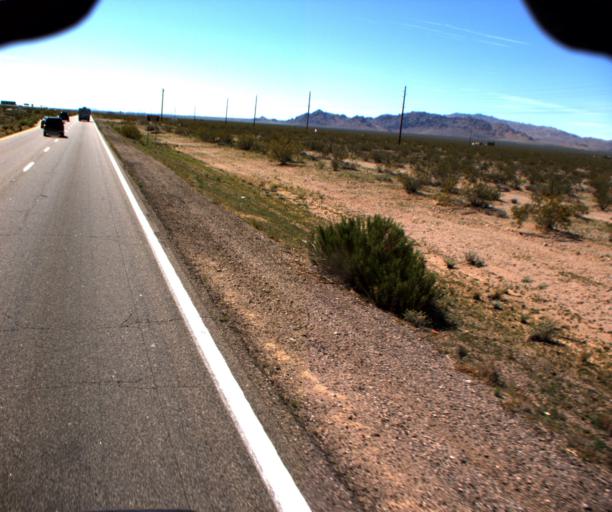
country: US
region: Arizona
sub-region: Mohave County
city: Dolan Springs
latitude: 35.7021
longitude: -114.4760
